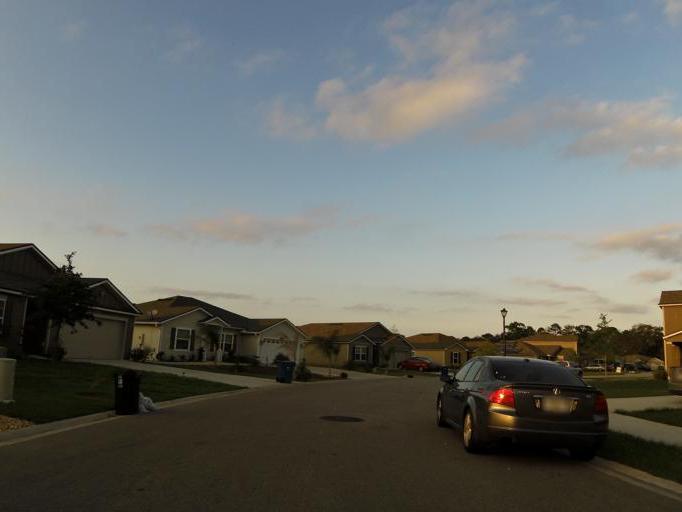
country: US
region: Florida
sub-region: Duval County
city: Jacksonville
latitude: 30.4705
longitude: -81.6243
